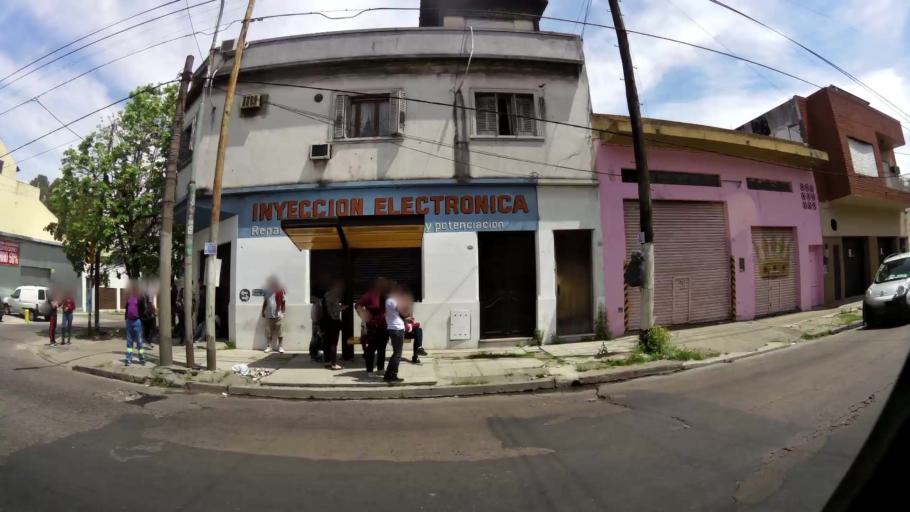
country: AR
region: Buenos Aires
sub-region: Partido de Lanus
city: Lanus
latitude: -34.6731
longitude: -58.4113
